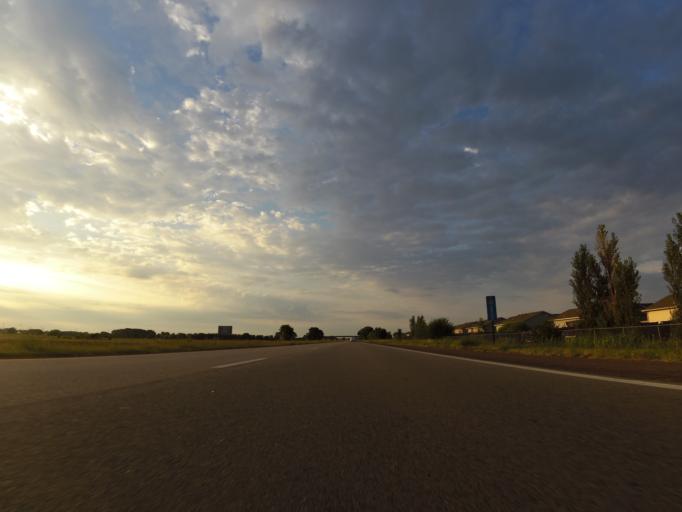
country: US
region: Kansas
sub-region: Sedgwick County
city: Maize
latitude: 37.7712
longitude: -97.4536
